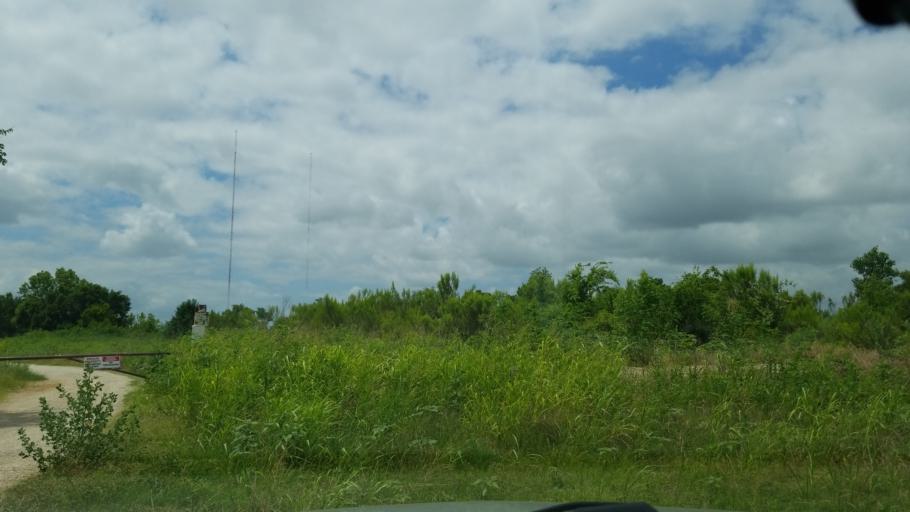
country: US
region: Texas
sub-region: Dallas County
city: Farmers Branch
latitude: 32.9496
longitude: -96.9401
